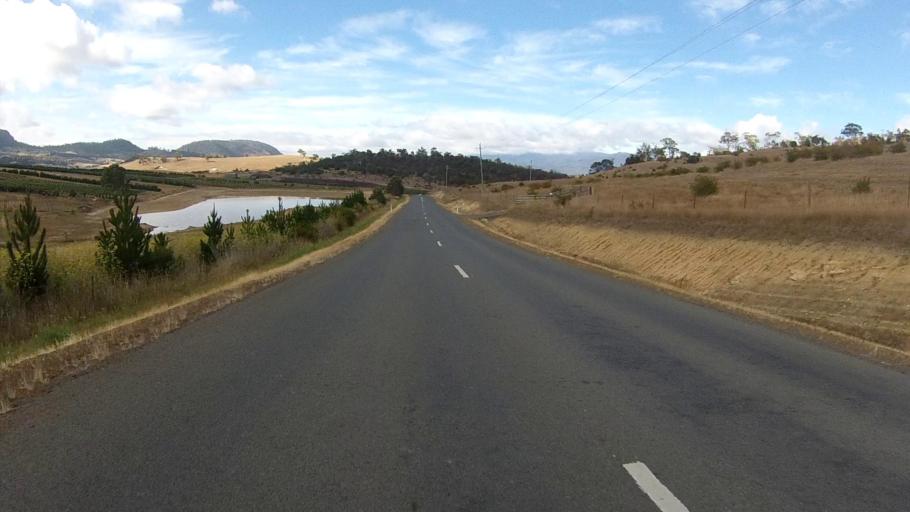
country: AU
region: Tasmania
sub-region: Brighton
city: Old Beach
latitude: -42.7371
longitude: 147.2885
